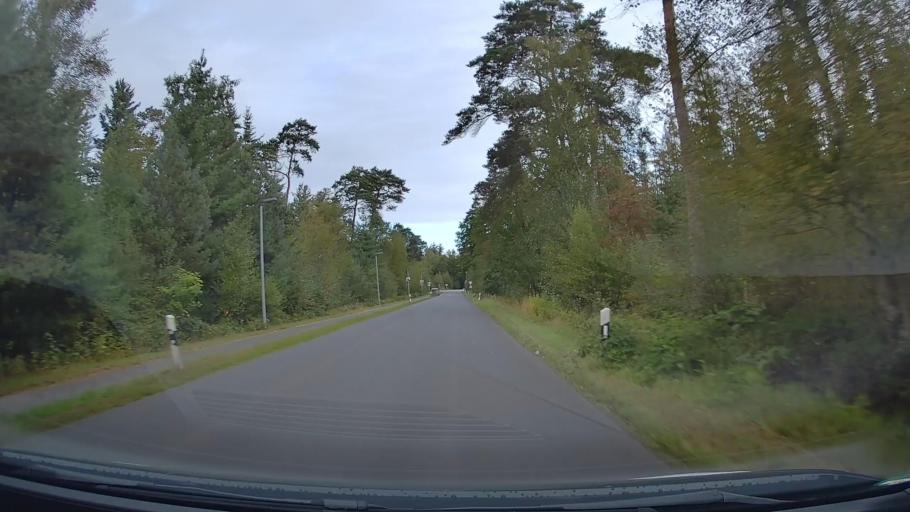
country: DE
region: Lower Saxony
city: Wardenburg
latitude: 53.1212
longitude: 8.1123
